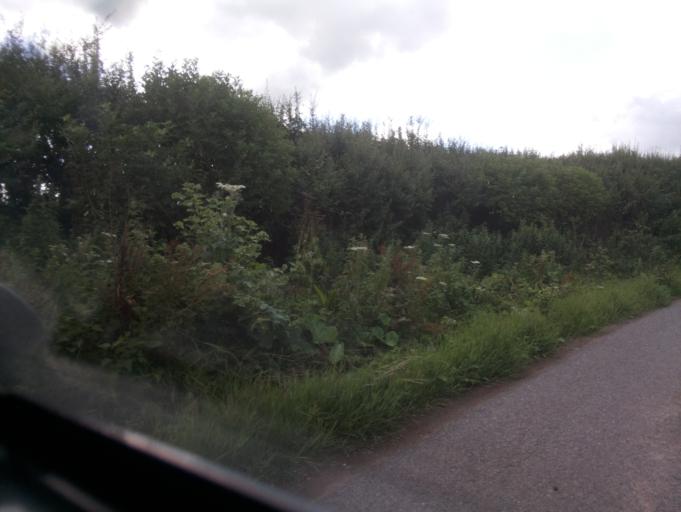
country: GB
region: England
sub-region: Gloucestershire
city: Newent
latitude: 51.8517
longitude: -2.3754
